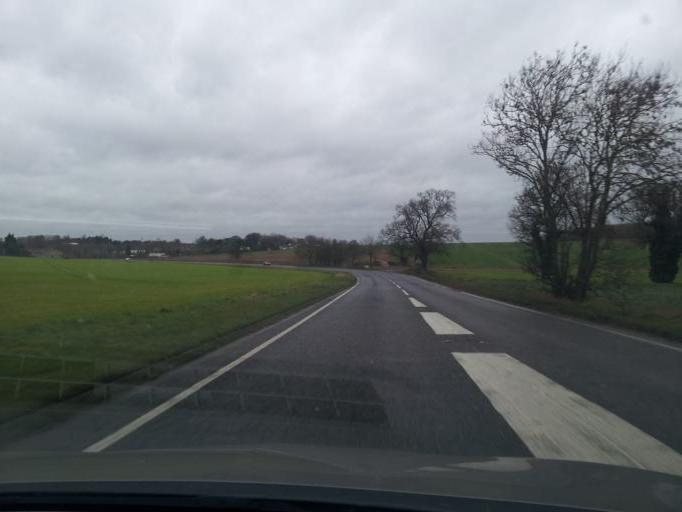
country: GB
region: England
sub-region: Suffolk
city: Botesdale
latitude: 52.3371
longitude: 0.9698
